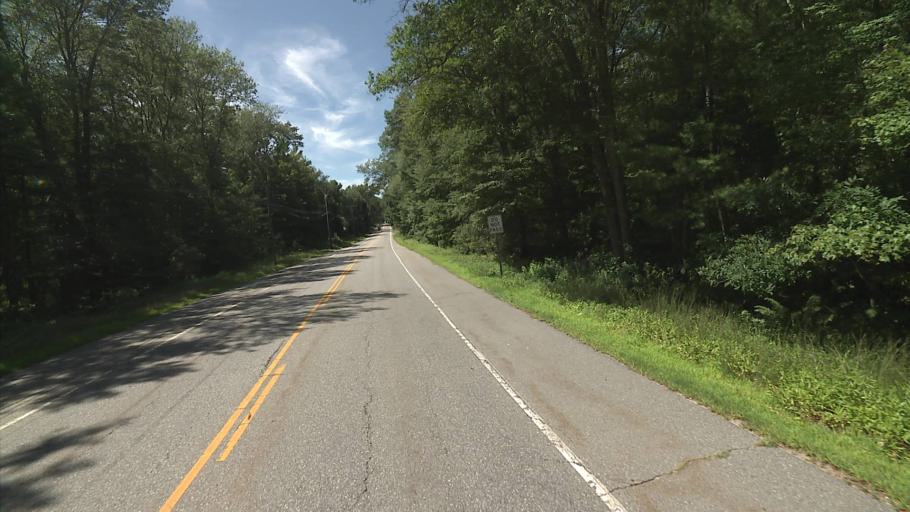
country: US
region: Connecticut
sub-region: Windham County
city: Killingly Center
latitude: 41.8485
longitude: -71.9071
